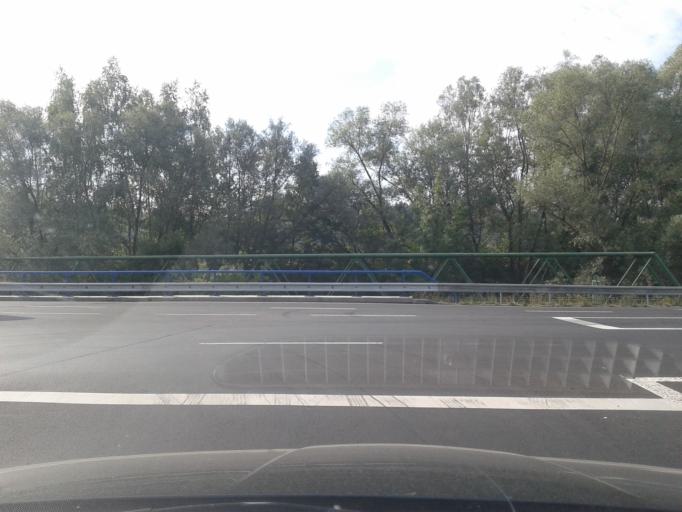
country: CZ
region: Moravskoslezsky
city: Havirov
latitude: 49.8032
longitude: 18.4427
